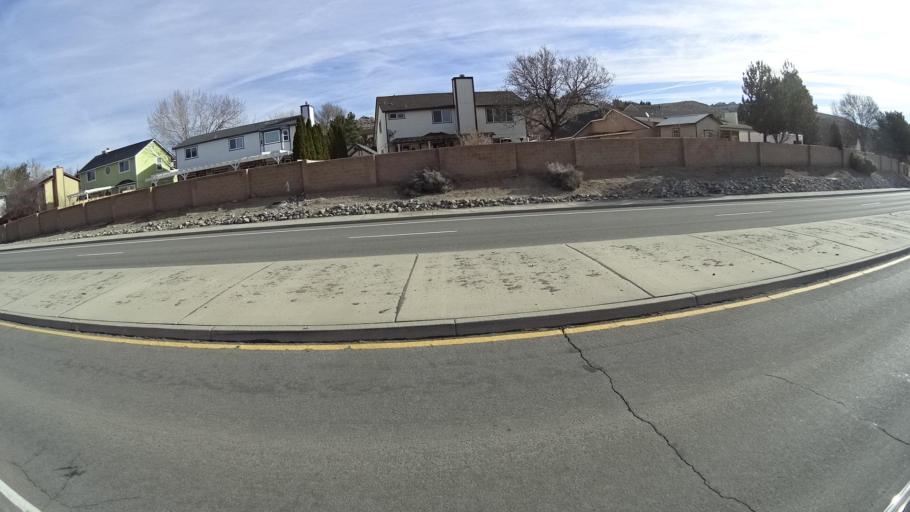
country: US
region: Nevada
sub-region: Washoe County
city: Sparks
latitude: 39.5690
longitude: -119.7168
